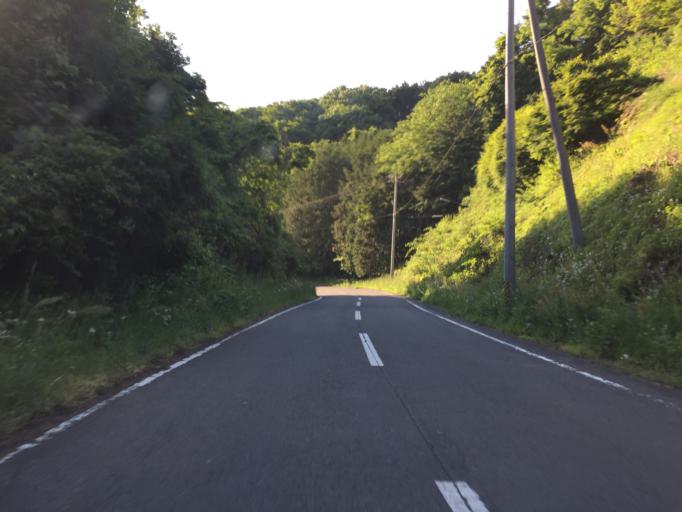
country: JP
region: Ibaraki
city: Daigo
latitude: 36.9275
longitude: 140.4520
